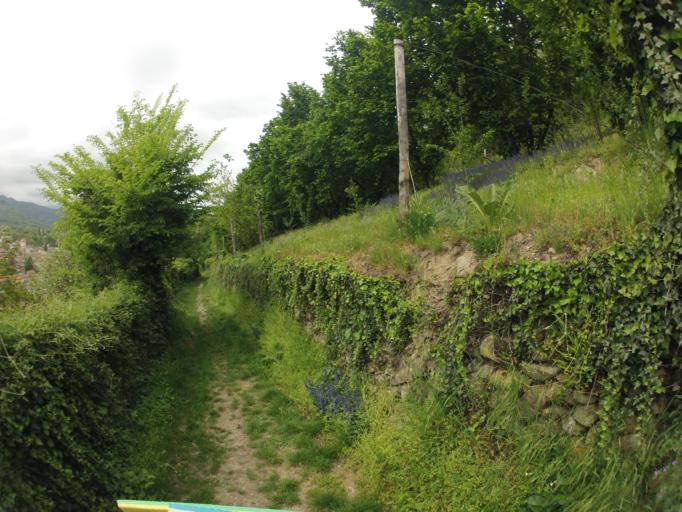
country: IT
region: Piedmont
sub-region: Provincia di Cuneo
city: Peveragno
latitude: 44.3332
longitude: 7.6166
